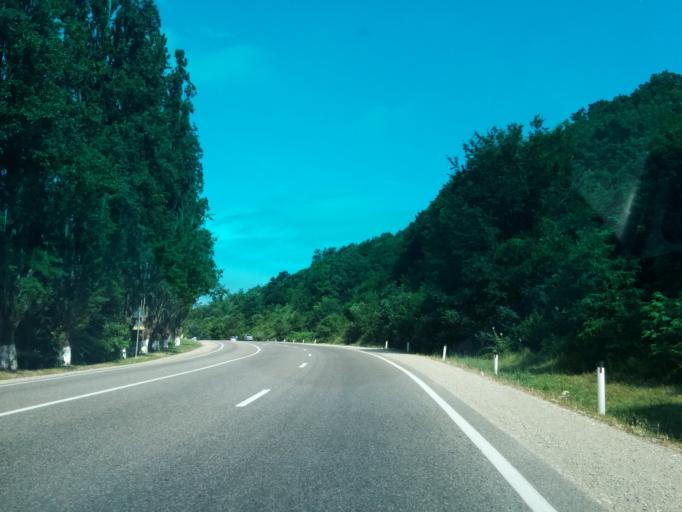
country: RU
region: Krasnodarskiy
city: Nebug
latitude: 44.1519
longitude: 39.0143
